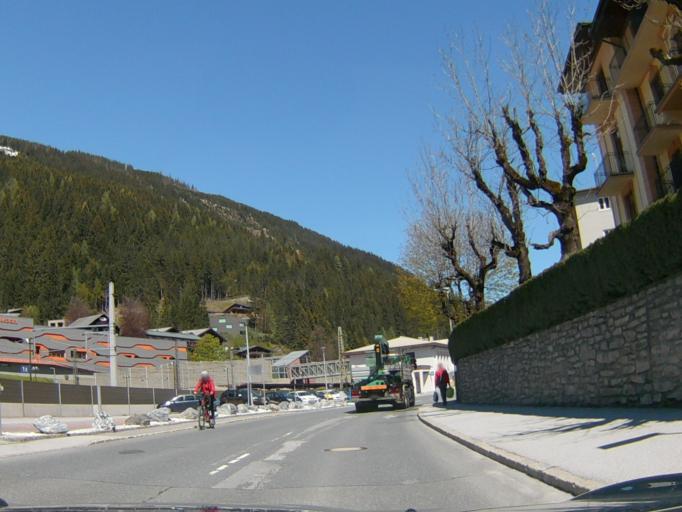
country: AT
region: Salzburg
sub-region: Politischer Bezirk Sankt Johann im Pongau
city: Bad Gastein
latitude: 47.1101
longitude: 13.1331
